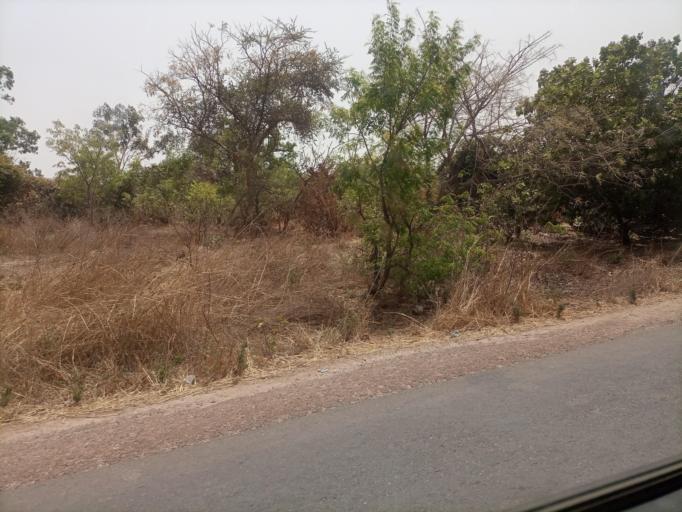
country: SN
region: Fatick
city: Sokone
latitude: 13.7204
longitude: -16.4252
